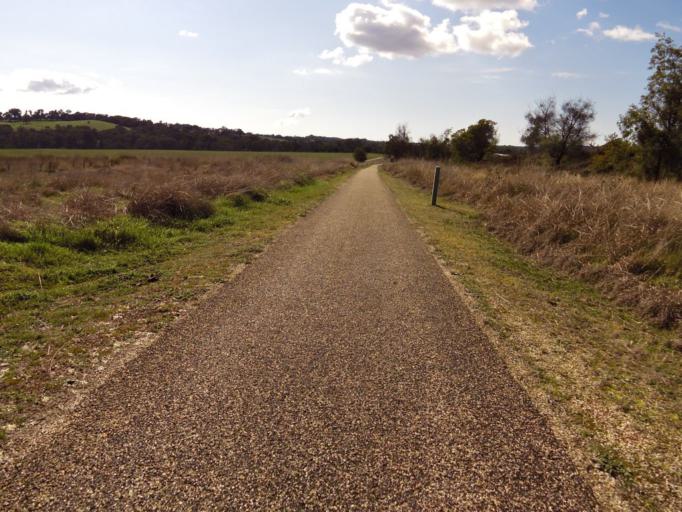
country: AU
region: Victoria
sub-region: Wangaratta
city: Wangaratta
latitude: -36.3972
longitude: 146.6522
